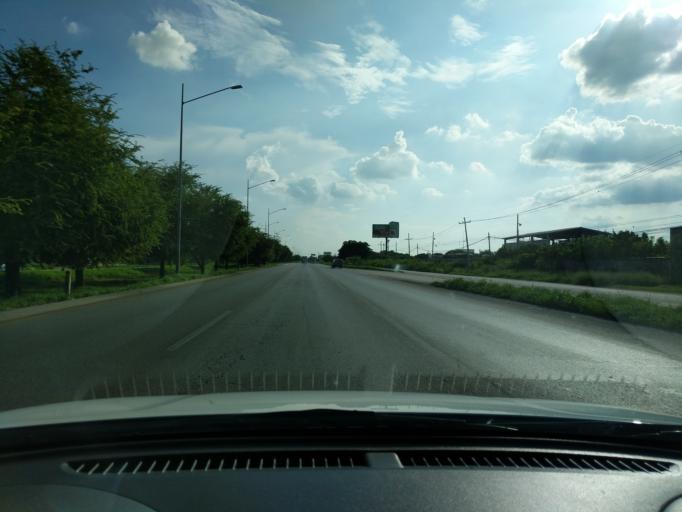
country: MX
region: Yucatan
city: Itzincab Palomeque
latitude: 20.9611
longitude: -89.6951
